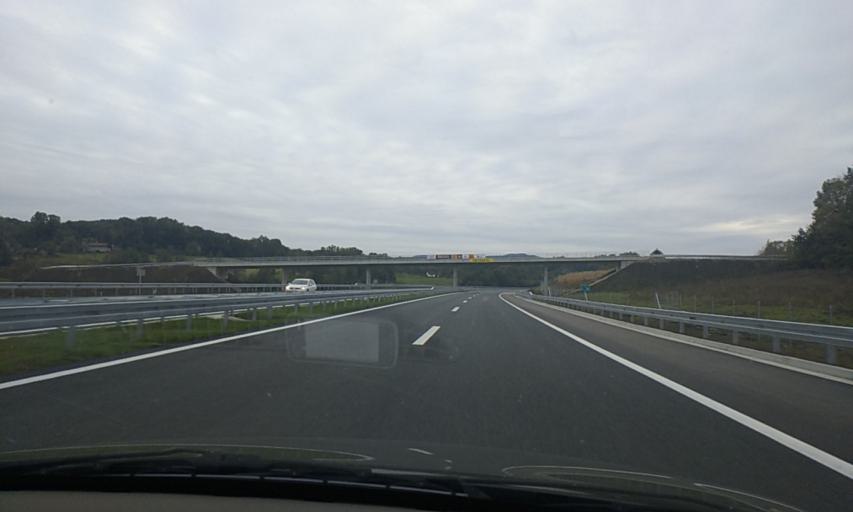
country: BA
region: Republika Srpska
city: Maglajani
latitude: 44.8654
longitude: 17.4930
